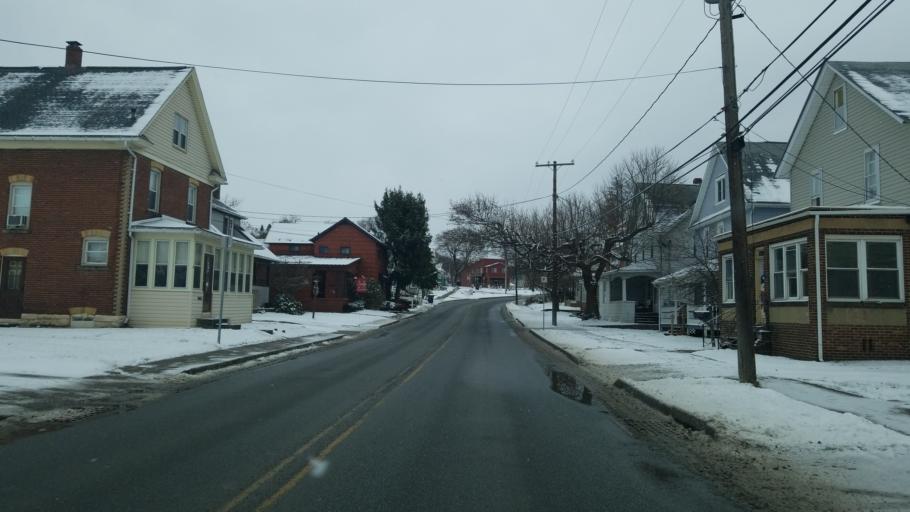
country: US
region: Pennsylvania
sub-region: Clearfield County
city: Sandy
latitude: 41.1115
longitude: -78.7729
